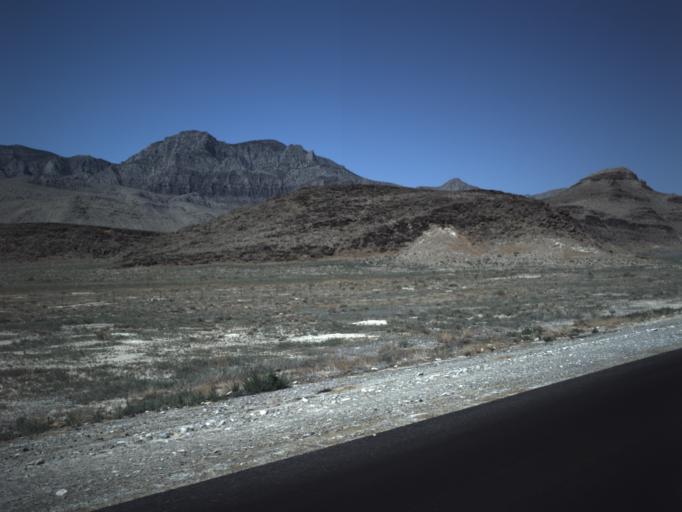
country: US
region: Utah
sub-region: Beaver County
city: Milford
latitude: 39.0555
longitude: -113.4287
